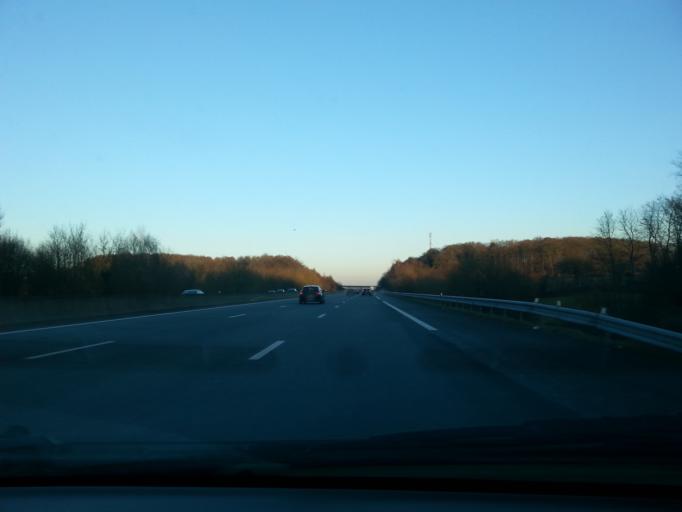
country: FR
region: Centre
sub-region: Departement d'Eure-et-Loir
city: Authon-du-Perche
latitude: 48.2012
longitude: 0.8845
